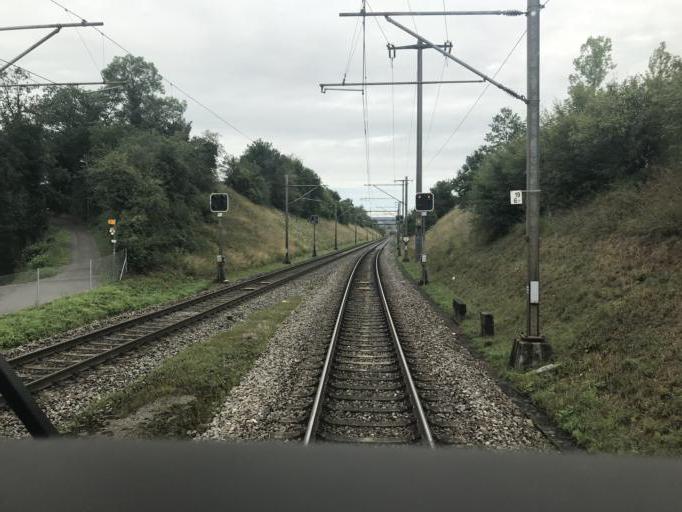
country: CH
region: Zurich
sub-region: Bezirk Buelach
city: Seglingen
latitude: 47.5505
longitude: 8.5238
